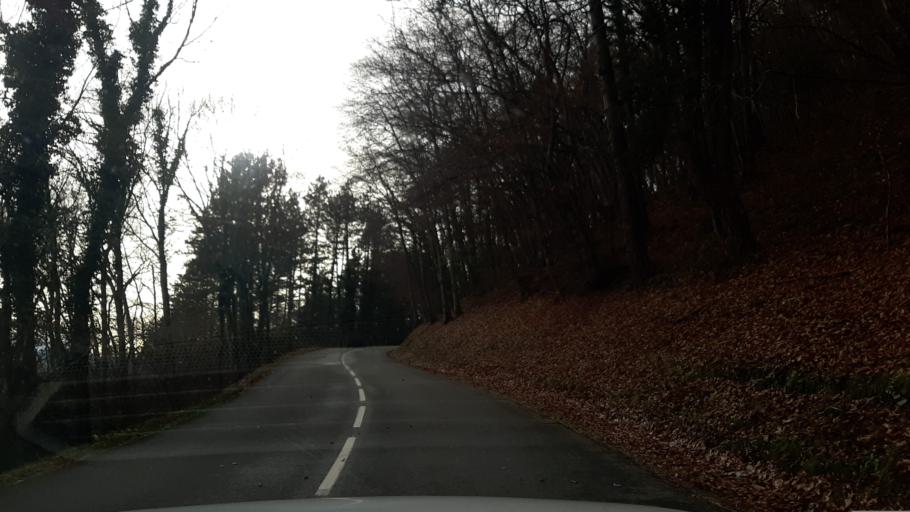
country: FR
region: Rhone-Alpes
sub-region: Departement de la Savoie
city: Coise-Saint-Jean-Pied-Gauthier
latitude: 45.5858
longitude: 6.1521
